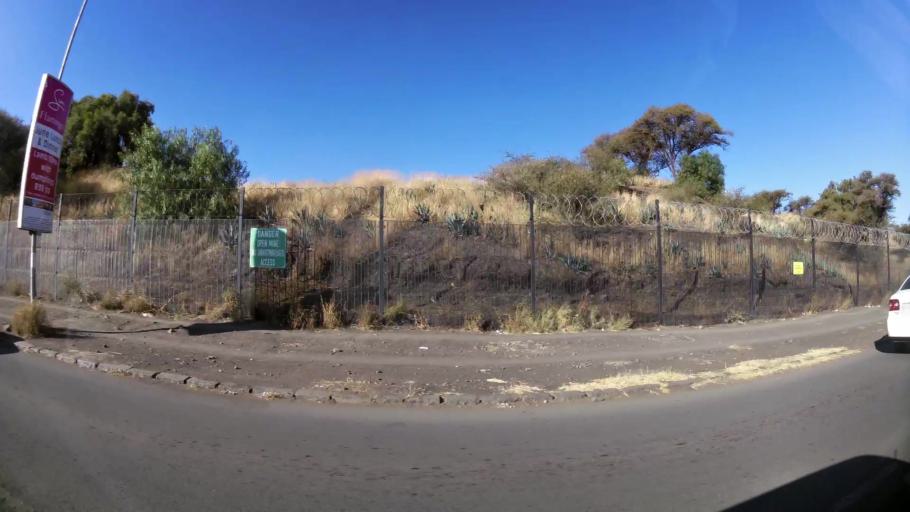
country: ZA
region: Northern Cape
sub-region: Frances Baard District Municipality
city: Kimberley
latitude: -28.7412
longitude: 24.7548
